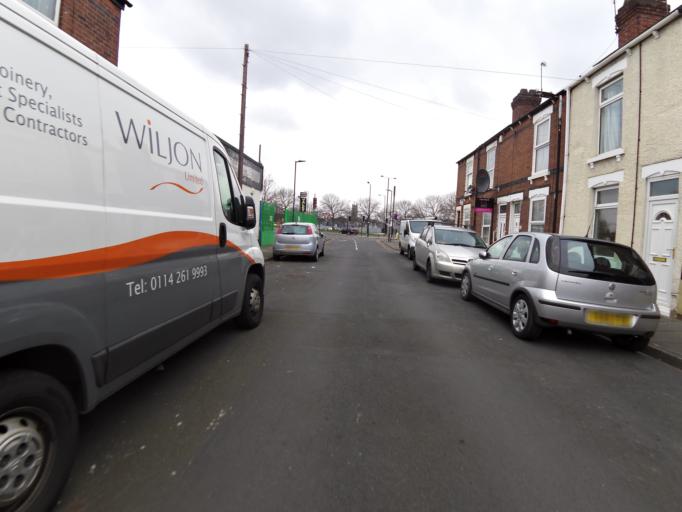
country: GB
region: England
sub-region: Doncaster
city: Doncaster
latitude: 53.5296
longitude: -1.1264
